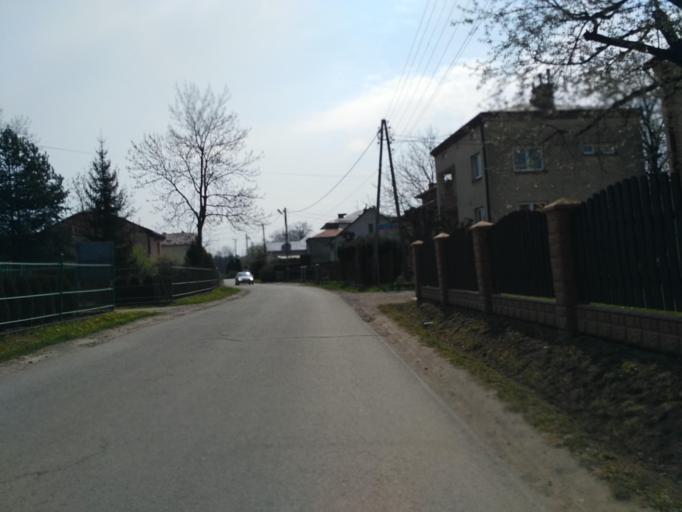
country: PL
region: Subcarpathian Voivodeship
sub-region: Krosno
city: Krosno
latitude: 49.6618
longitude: 21.7510
